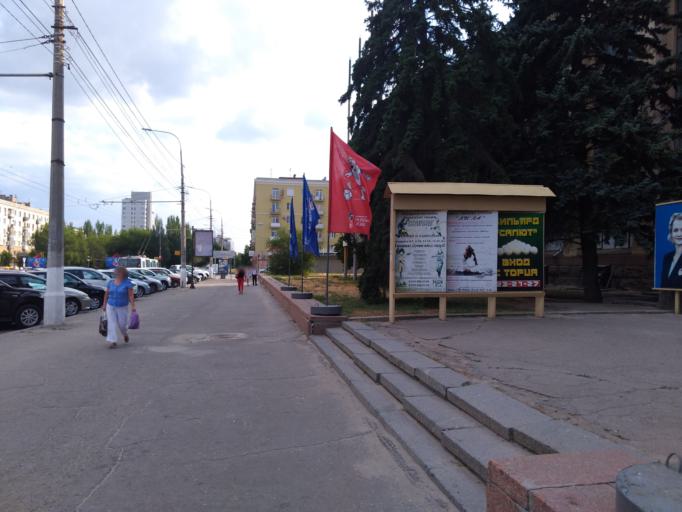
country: RU
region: Volgograd
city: Volgograd
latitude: 48.7170
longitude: 44.5292
